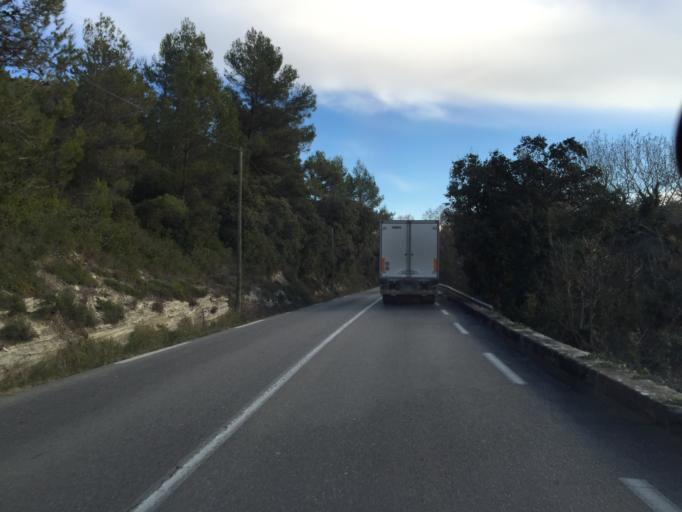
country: FR
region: Provence-Alpes-Cote d'Azur
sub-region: Departement du Vaucluse
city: Goult
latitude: 43.8603
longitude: 5.2250
